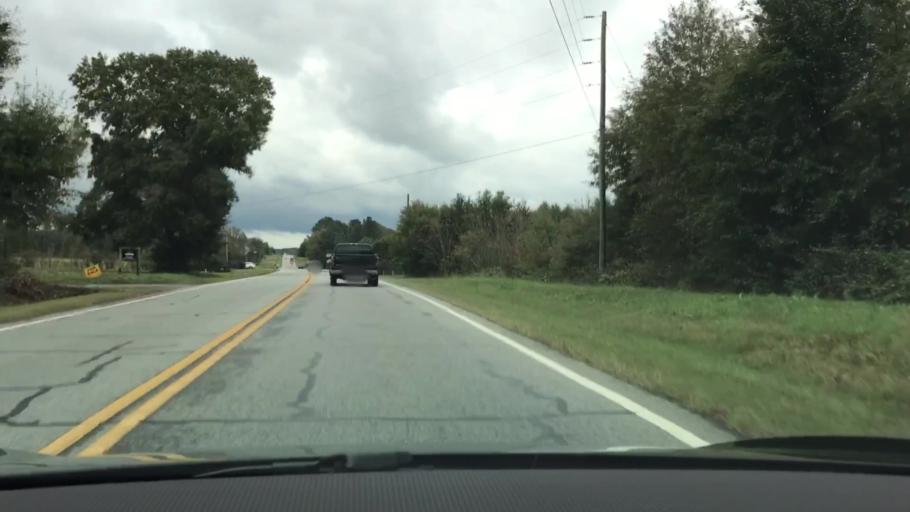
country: US
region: Georgia
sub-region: Oconee County
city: Watkinsville
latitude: 33.8364
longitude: -83.3829
